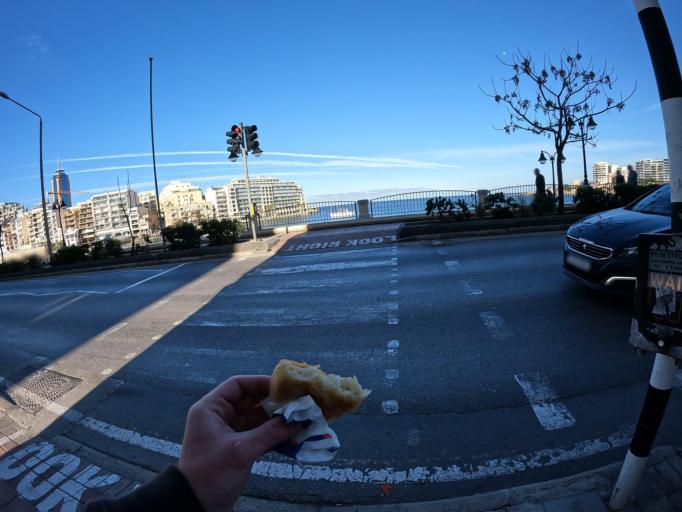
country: MT
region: Saint Julian
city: San Giljan
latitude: 35.9172
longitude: 14.4932
